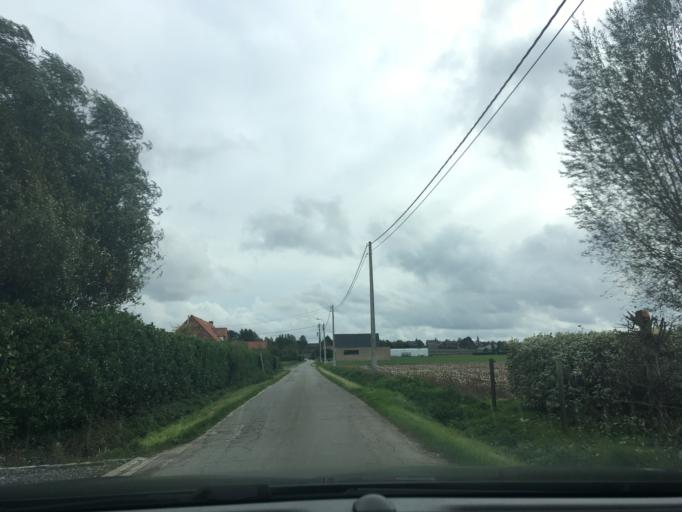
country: BE
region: Flanders
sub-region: Provincie West-Vlaanderen
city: Moorslede
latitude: 50.9021
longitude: 3.0539
